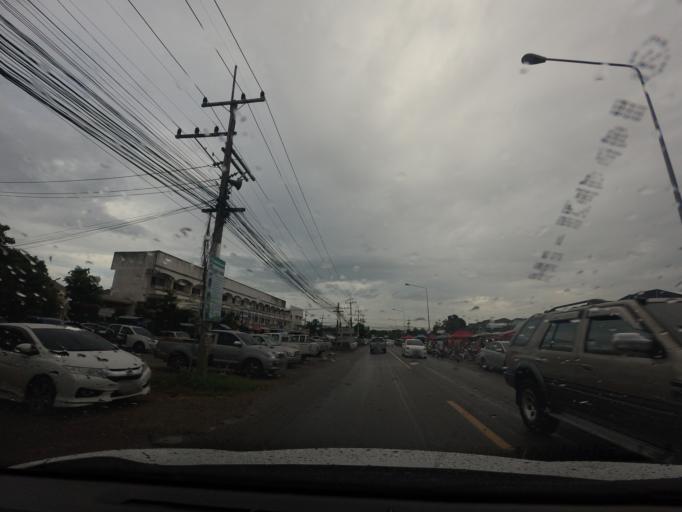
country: TH
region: Chon Buri
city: Sattahip
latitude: 12.6682
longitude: 100.9494
